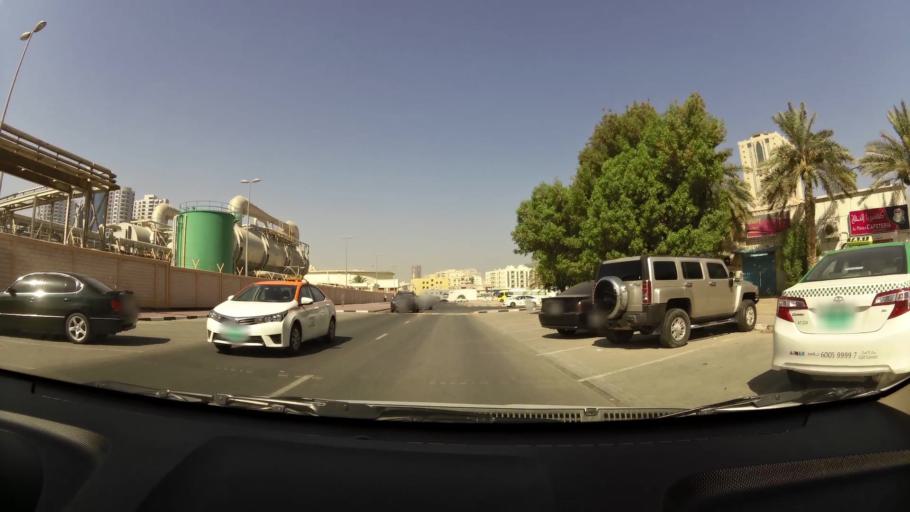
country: AE
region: Ajman
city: Ajman
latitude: 25.4034
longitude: 55.4503
